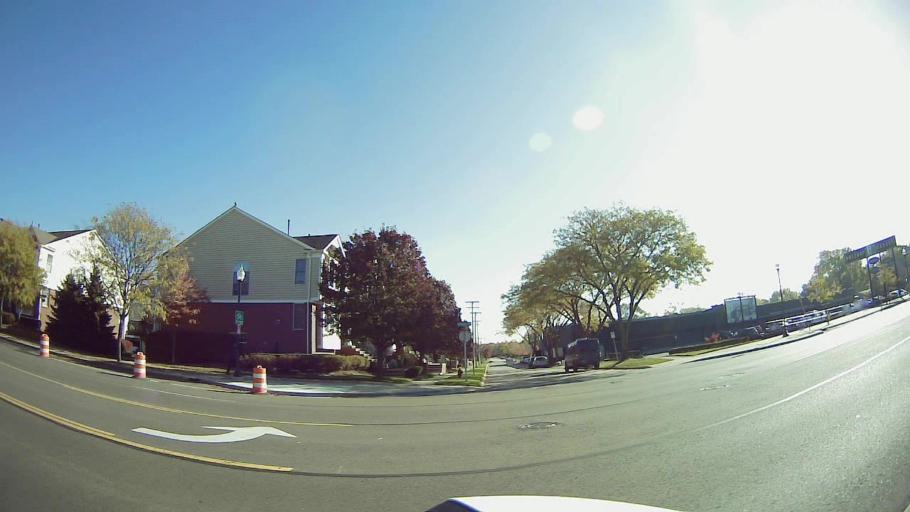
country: US
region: Michigan
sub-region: Oakland County
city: Pleasant Ridge
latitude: 42.4798
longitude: -83.1440
